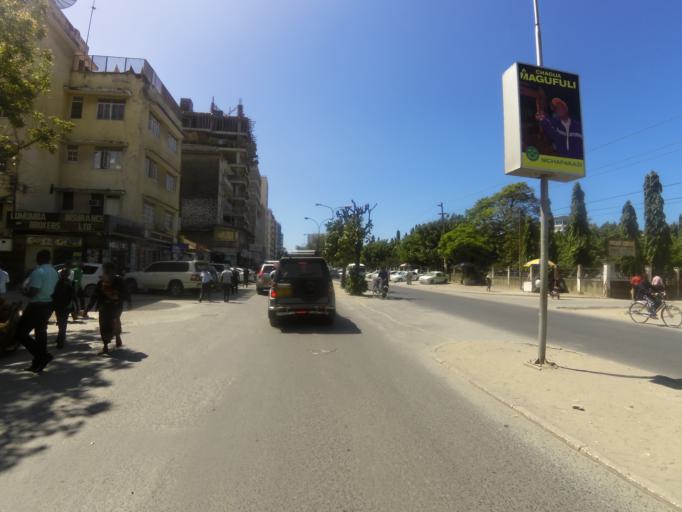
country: TZ
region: Dar es Salaam
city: Dar es Salaam
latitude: -6.8207
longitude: 39.2797
